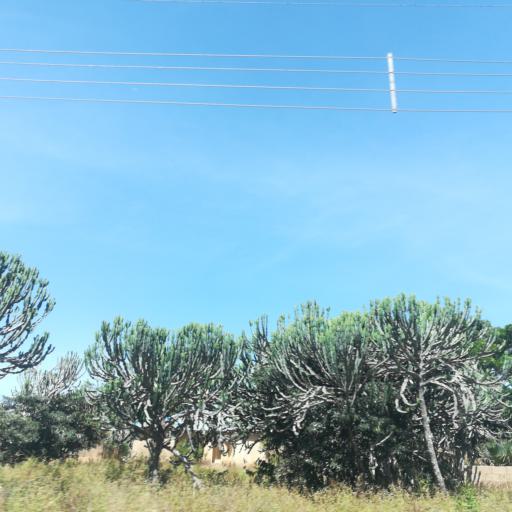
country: NG
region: Plateau
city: Bukuru
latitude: 9.7585
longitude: 8.8790
